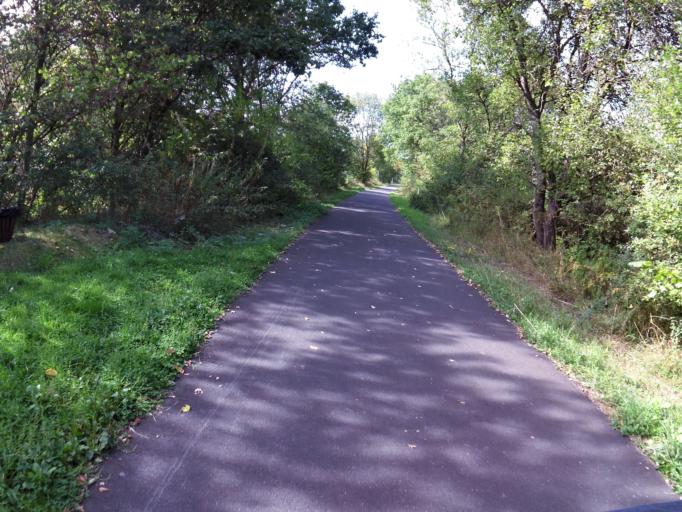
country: DE
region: Rheinland-Pfalz
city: Pronsfeld
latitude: 50.1595
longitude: 6.3284
